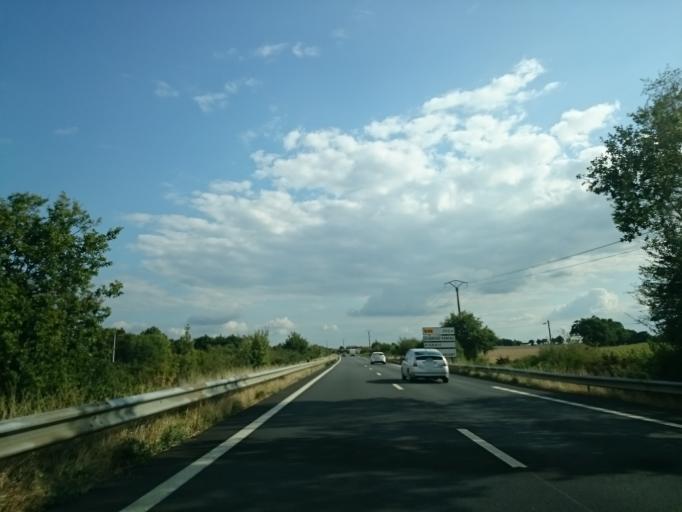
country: FR
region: Brittany
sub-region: Departement d'Ille-et-Vilaine
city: Grand-Fougeray
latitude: 47.6983
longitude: -1.7035
